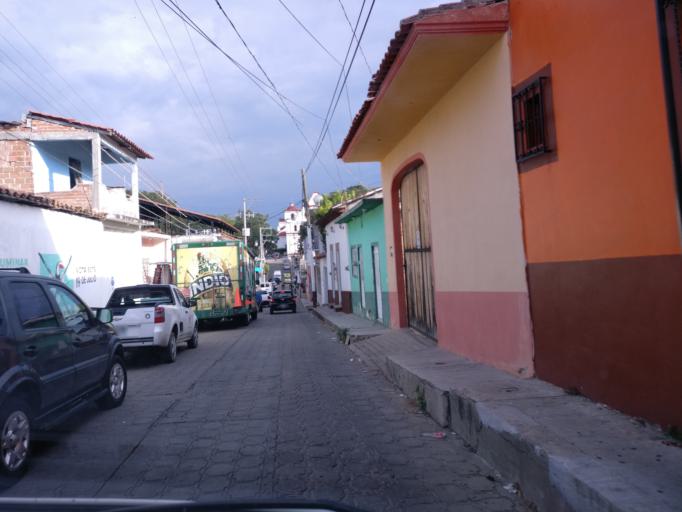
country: MX
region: Chiapas
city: Chiapa de Corzo
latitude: 16.7080
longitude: -93.0195
